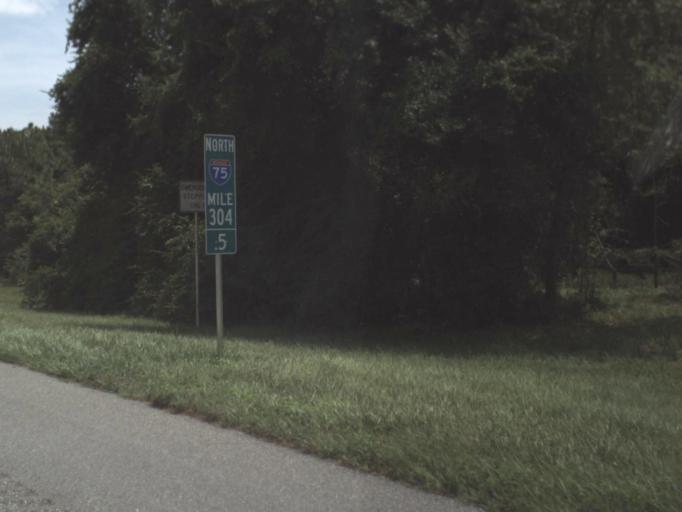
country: US
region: Florida
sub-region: Hernando County
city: Ridge Manor
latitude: 28.5698
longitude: -82.2278
